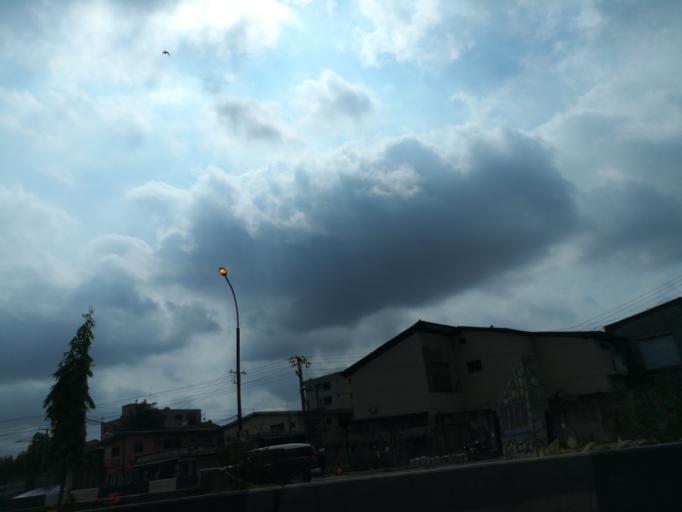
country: NG
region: Lagos
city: Ojota
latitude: 6.5618
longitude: 3.3956
